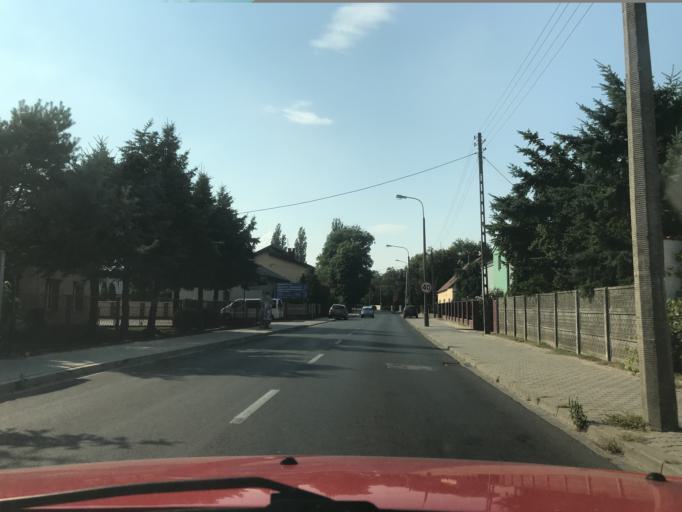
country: PL
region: Greater Poland Voivodeship
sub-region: Powiat poznanski
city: Plewiska
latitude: 52.3675
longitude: 16.8491
